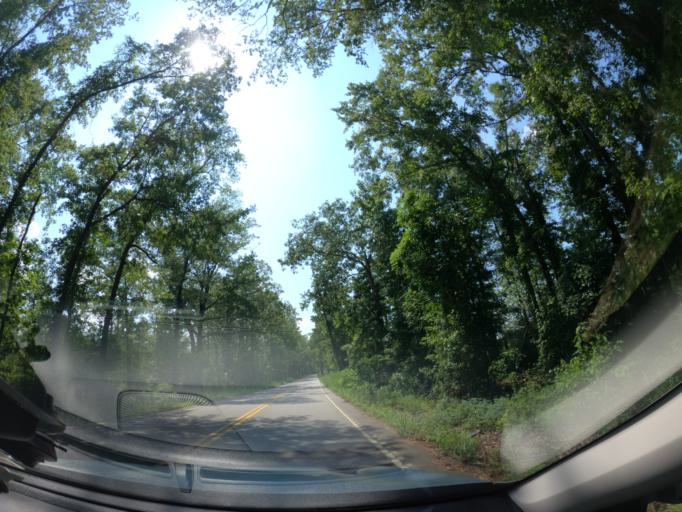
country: US
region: South Carolina
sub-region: Richland County
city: Hopkins
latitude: 33.8401
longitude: -80.8453
